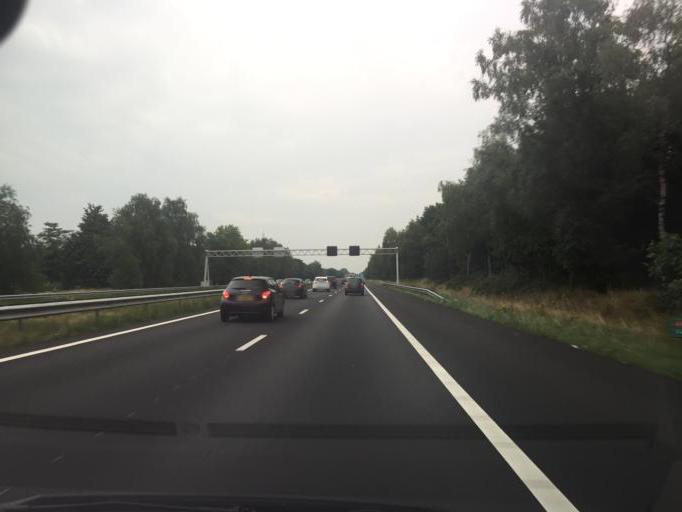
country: NL
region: North Brabant
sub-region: Gemeente Geldrop-Mierlo
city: Mierlo
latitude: 51.4237
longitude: 5.6562
